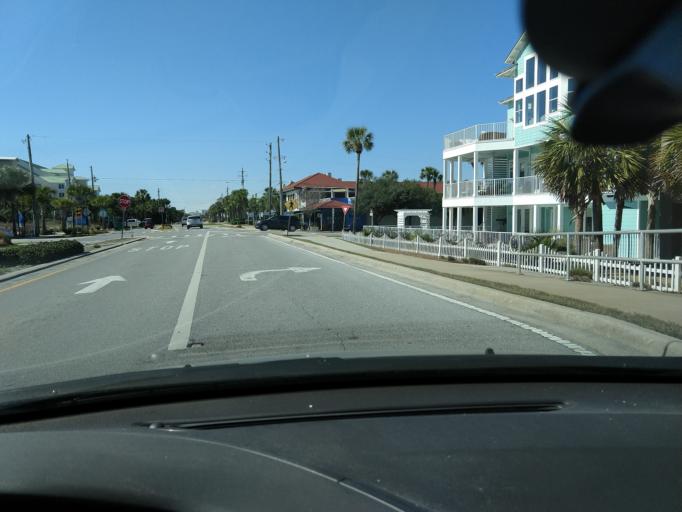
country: US
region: Florida
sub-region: Walton County
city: Miramar Beach
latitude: 30.3828
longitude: -86.4256
